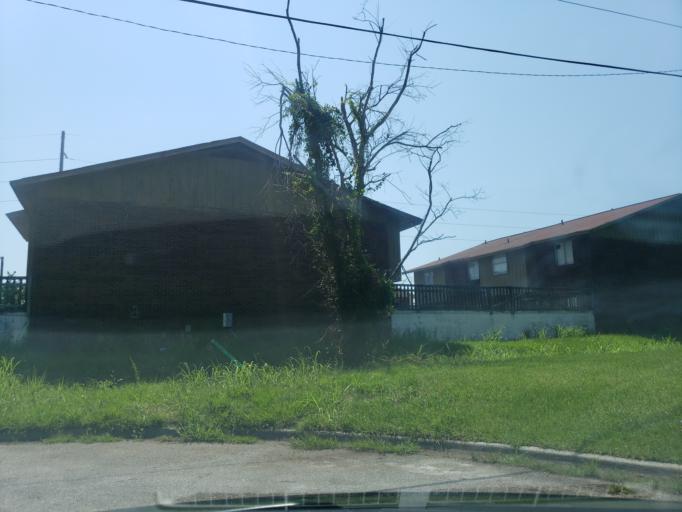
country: US
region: Georgia
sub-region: Chatham County
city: Montgomery
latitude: 31.9960
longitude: -81.1323
